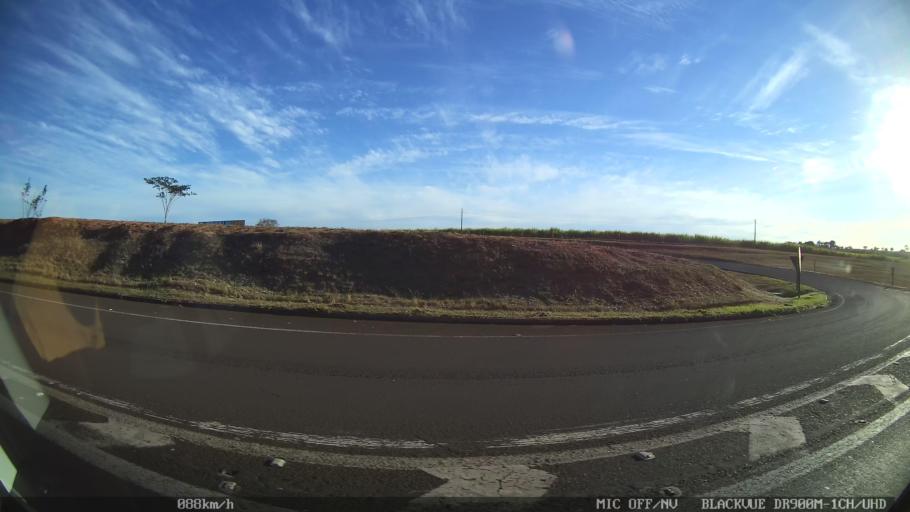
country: BR
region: Sao Paulo
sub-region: Sao Jose Do Rio Preto
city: Sao Jose do Rio Preto
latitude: -20.9048
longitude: -49.2962
